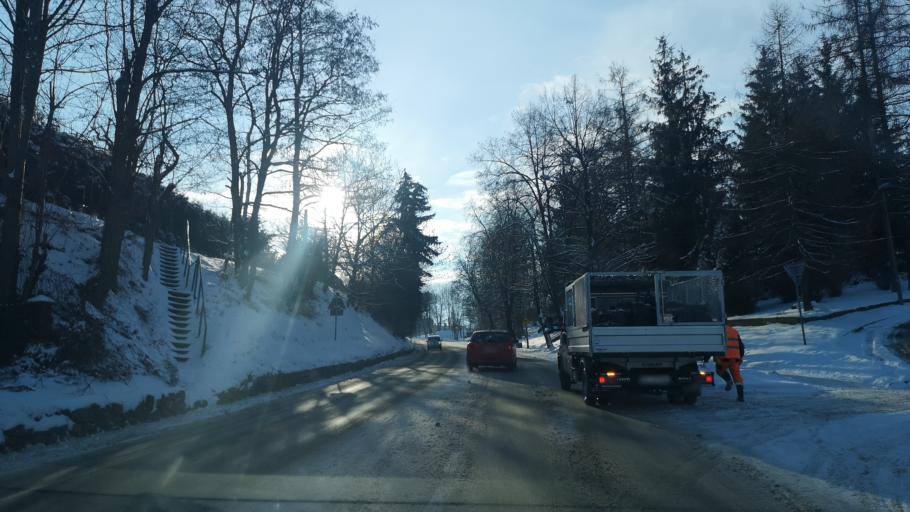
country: PL
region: Subcarpathian Voivodeship
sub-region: Powiat przeworski
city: Przeworsk
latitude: 50.0631
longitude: 22.4917
